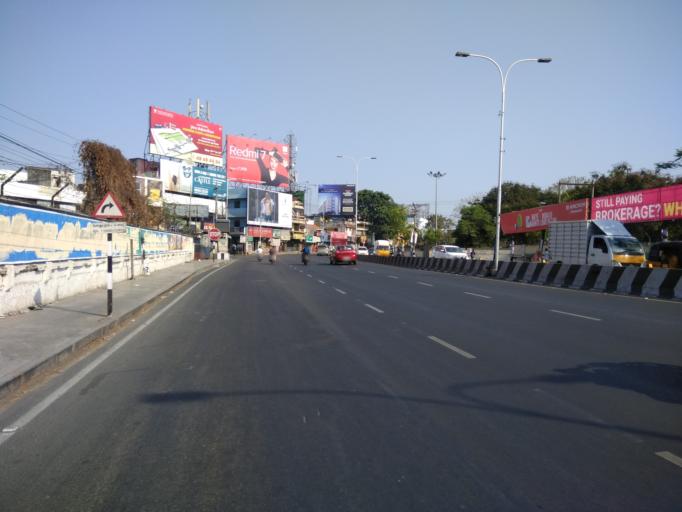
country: IN
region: Tamil Nadu
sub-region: Kancheepuram
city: Saint Thomas Mount
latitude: 13.0113
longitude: 80.1956
